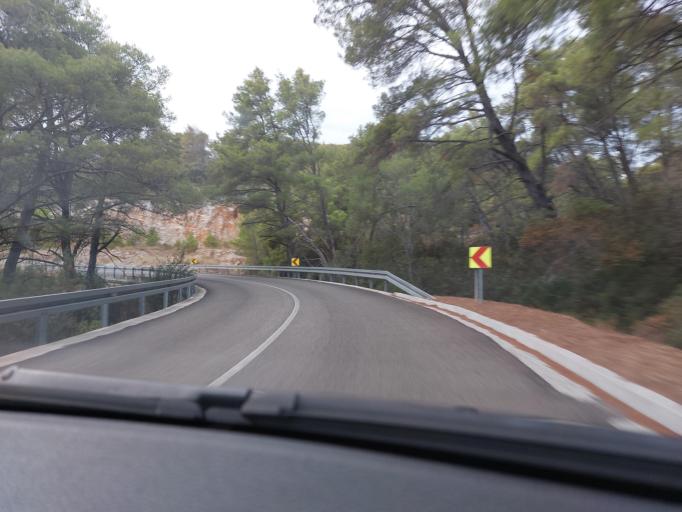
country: HR
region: Dubrovacko-Neretvanska
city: Smokvica
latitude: 42.7609
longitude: 16.8529
